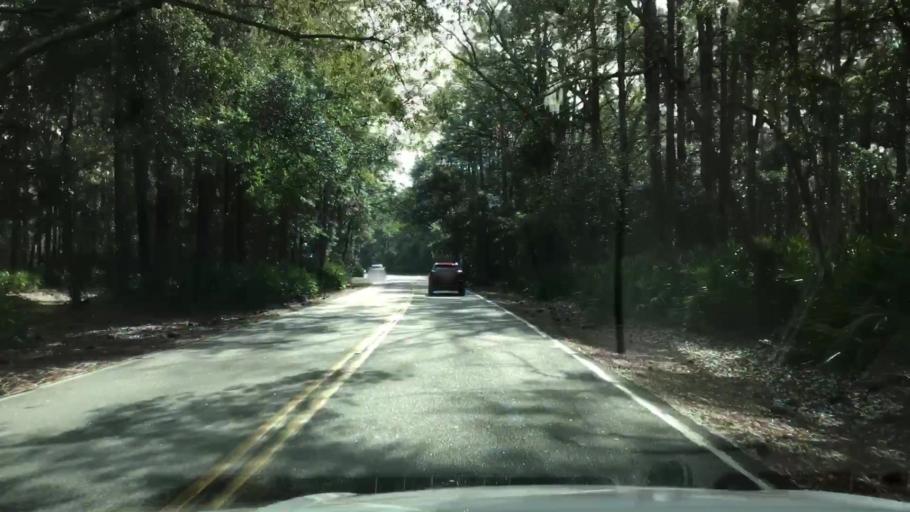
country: US
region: South Carolina
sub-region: Beaufort County
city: Hilton Head Island
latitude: 32.2353
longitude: -80.7241
